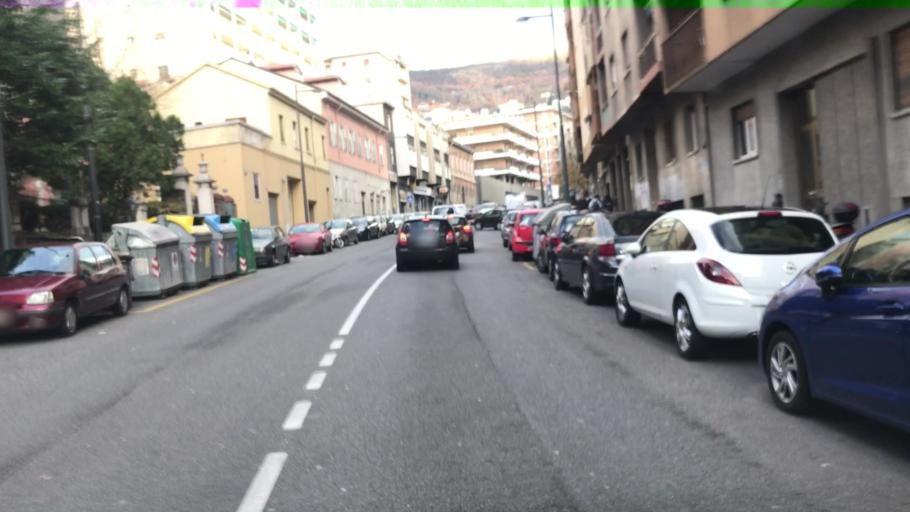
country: IT
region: Friuli Venezia Giulia
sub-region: Provincia di Trieste
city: Trieste
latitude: 45.6574
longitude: 13.7886
